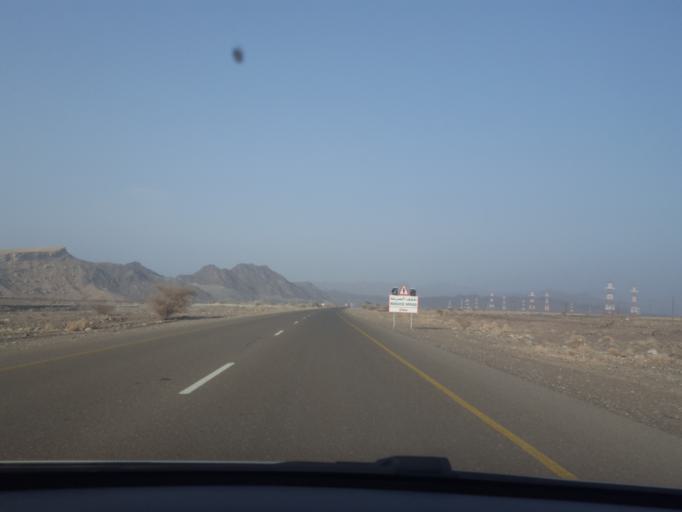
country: AE
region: Abu Dhabi
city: Al Ain
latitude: 24.0450
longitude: 56.0367
